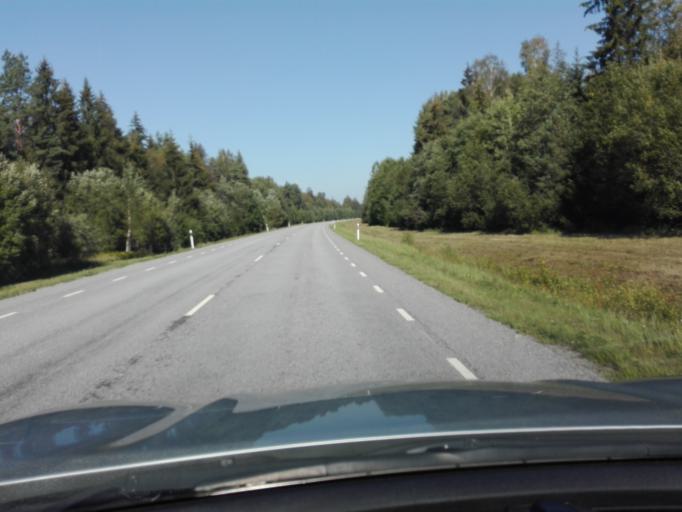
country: EE
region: Raplamaa
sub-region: Rapla vald
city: Rapla
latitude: 59.0075
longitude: 24.7697
